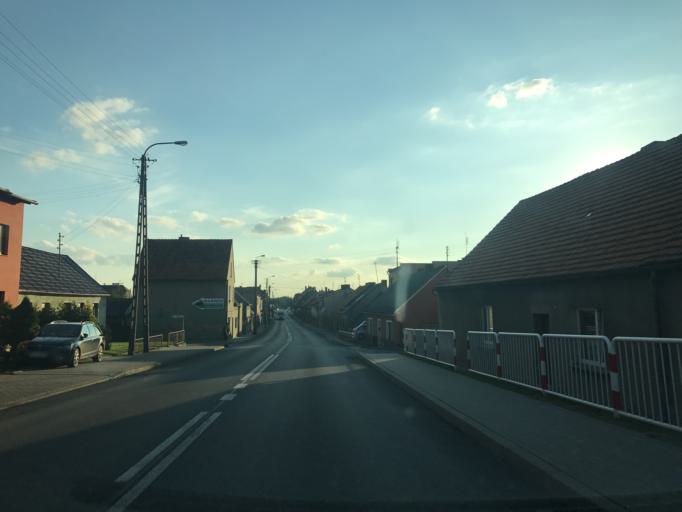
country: PL
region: Greater Poland Voivodeship
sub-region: Powiat gostynski
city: Piaski
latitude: 51.8849
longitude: 17.0750
